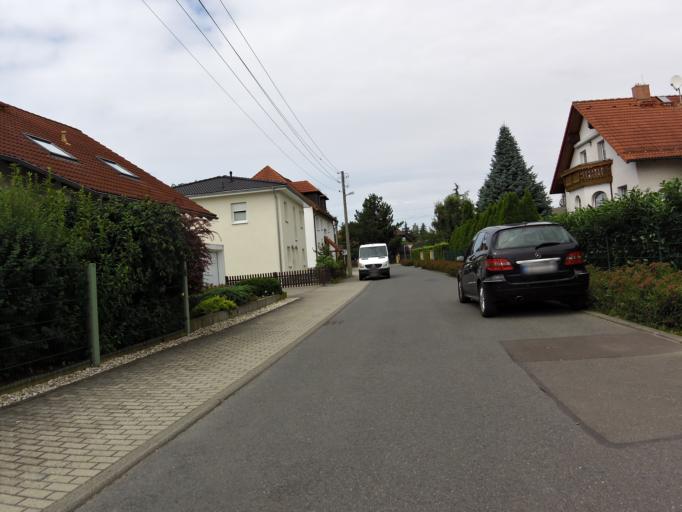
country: DE
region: Saxony
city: Rackwitz
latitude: 51.3990
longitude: 12.3729
